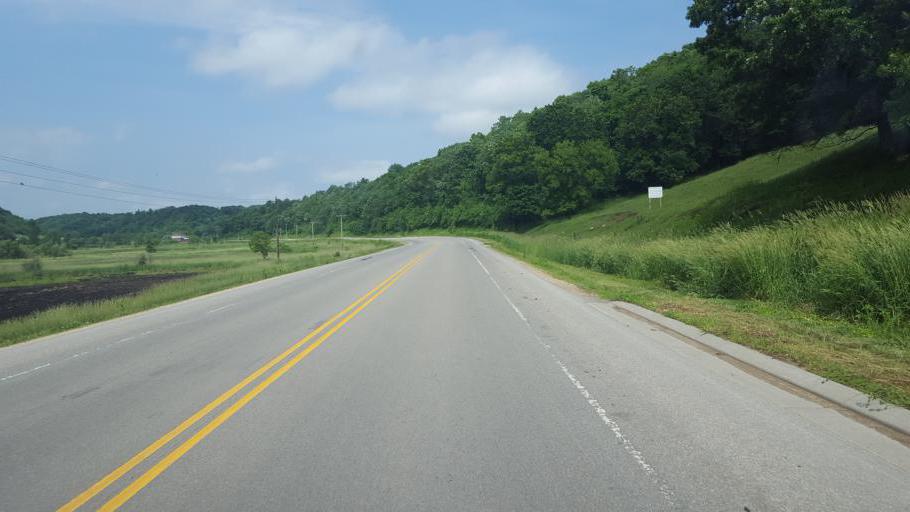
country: US
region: Wisconsin
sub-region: Monroe County
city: Cashton
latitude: 43.7343
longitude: -90.6942
